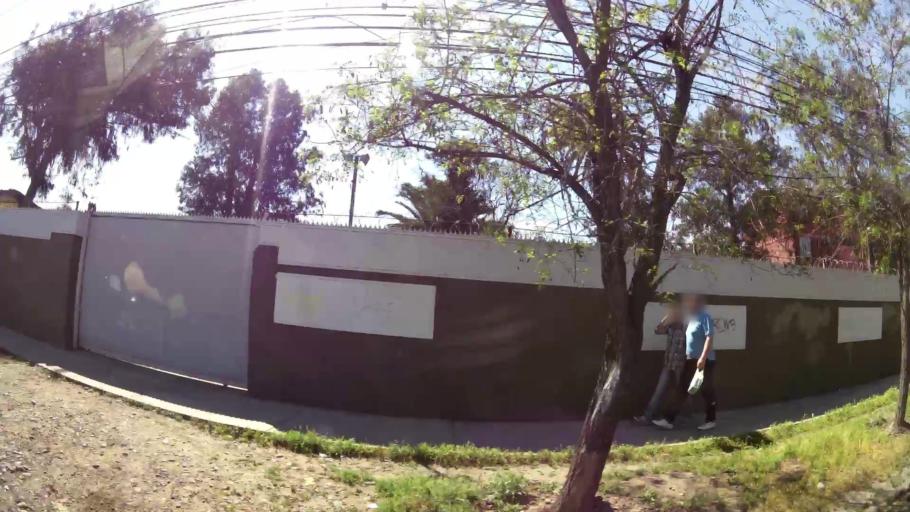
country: CL
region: Santiago Metropolitan
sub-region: Provincia de Santiago
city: La Pintana
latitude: -33.5272
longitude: -70.6568
